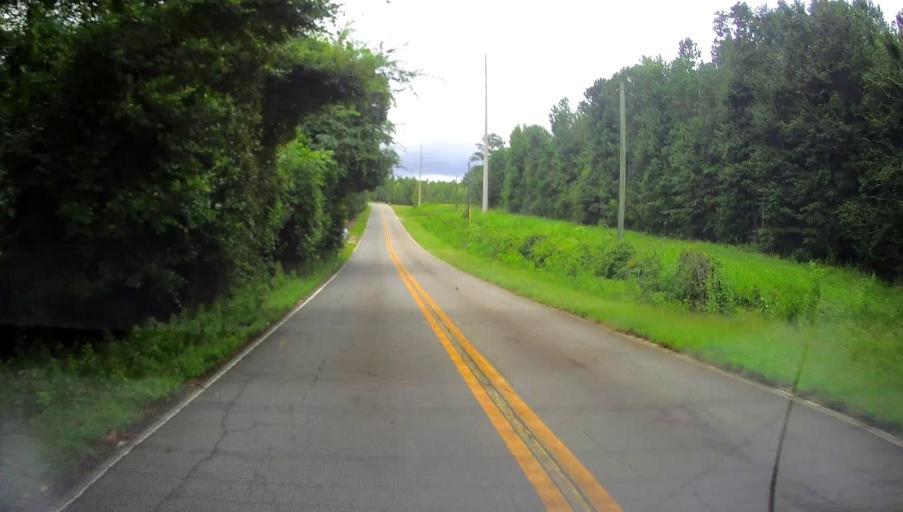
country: US
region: Georgia
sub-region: Bibb County
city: Macon
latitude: 32.7903
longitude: -83.5168
